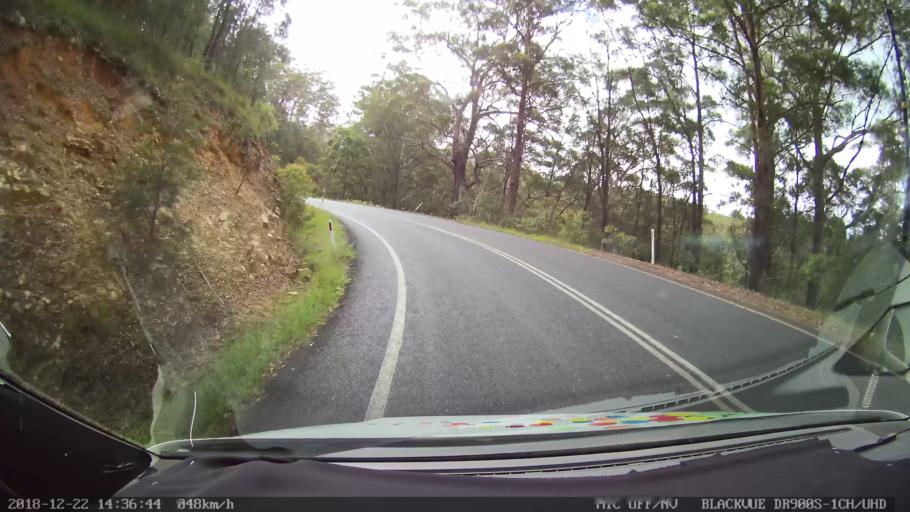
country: AU
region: New South Wales
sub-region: Bellingen
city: Dorrigo
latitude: -30.1301
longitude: 152.6042
